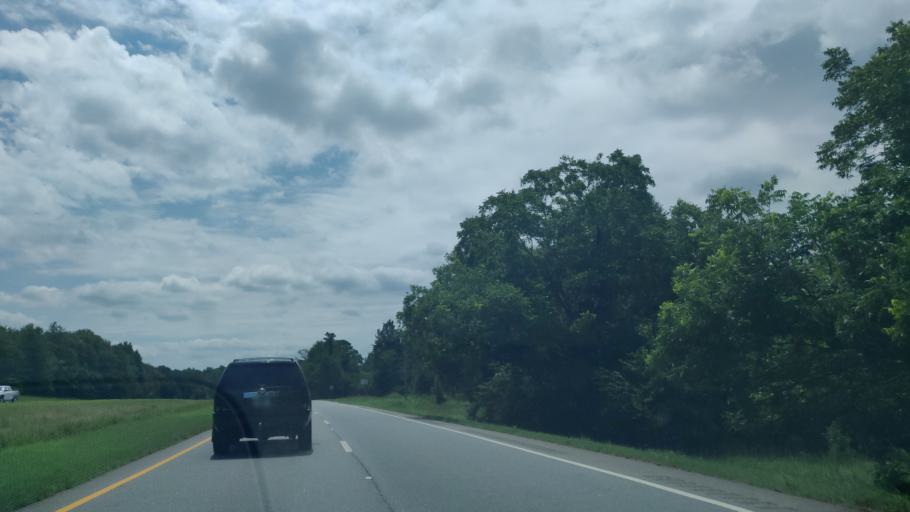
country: US
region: Georgia
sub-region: Terrell County
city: Dawson
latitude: 31.8723
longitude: -84.4937
